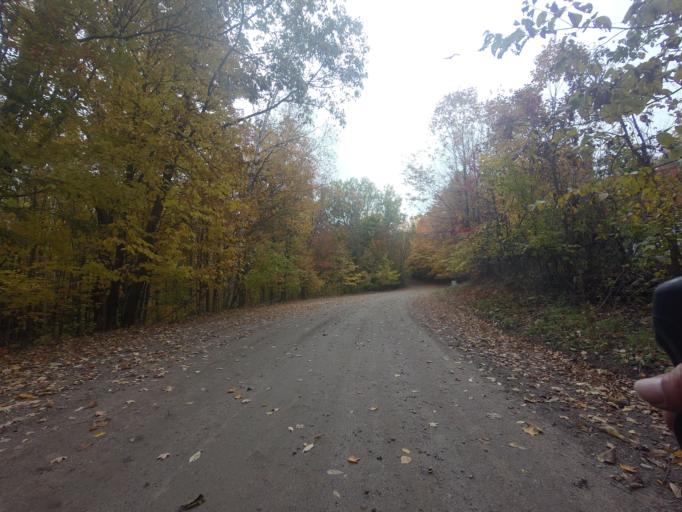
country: CA
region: Ontario
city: Pembroke
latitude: 45.7315
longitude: -77.2276
